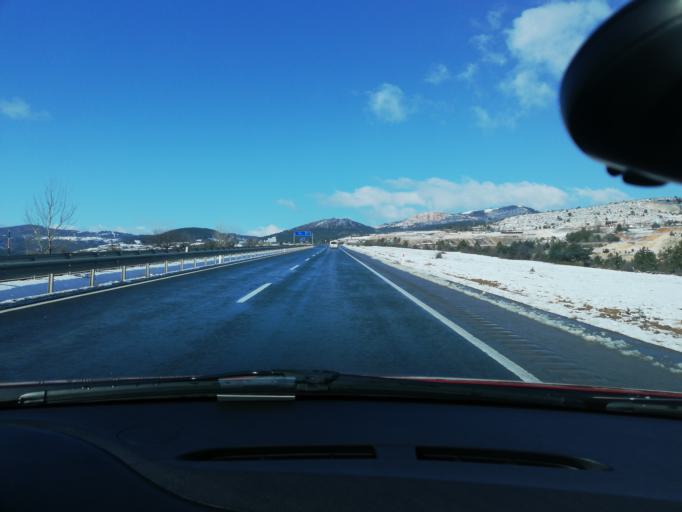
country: TR
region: Kastamonu
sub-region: Cide
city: Kastamonu
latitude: 41.3642
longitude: 33.7322
